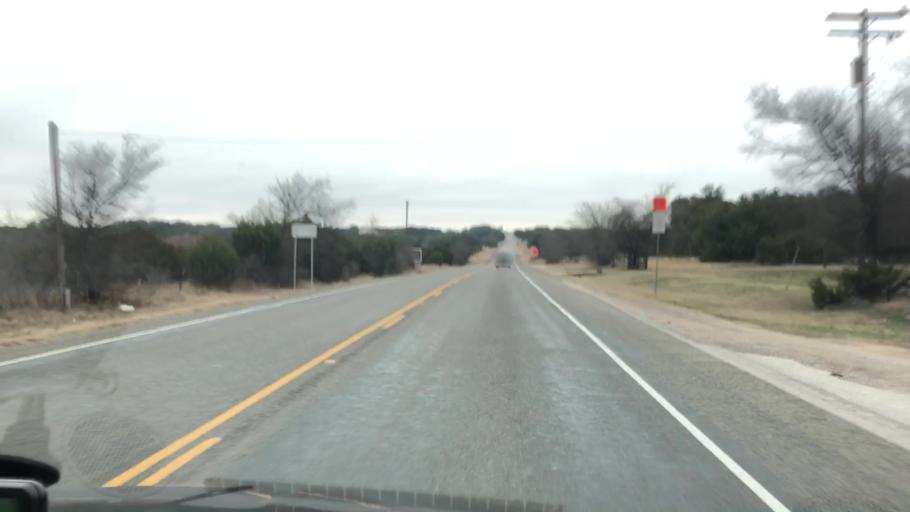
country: US
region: Texas
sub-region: Hamilton County
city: Hico
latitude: 31.9942
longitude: -98.0449
